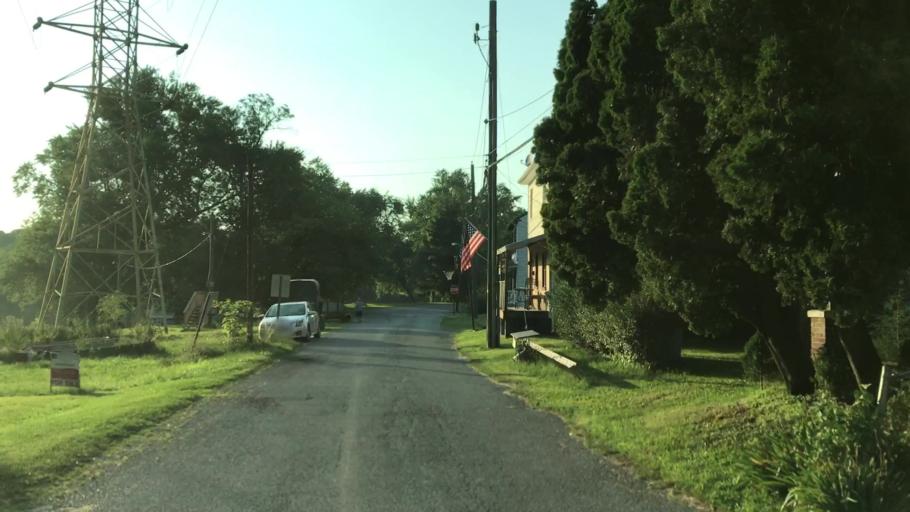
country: US
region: Pennsylvania
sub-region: Dauphin County
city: Middletown
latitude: 40.1849
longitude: -76.7309
